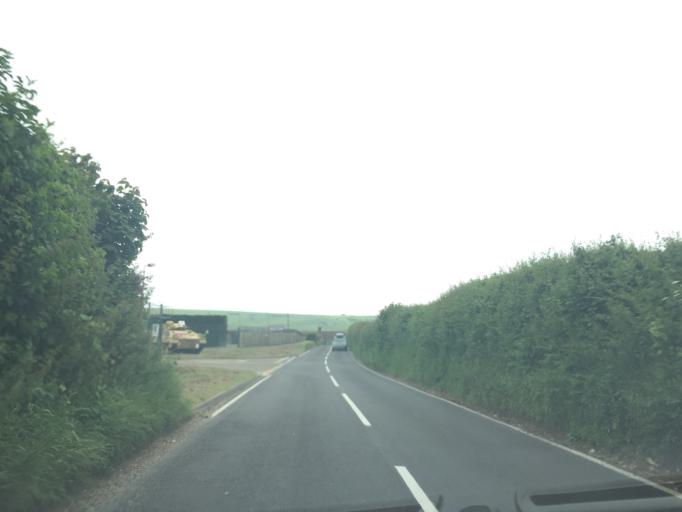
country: GB
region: England
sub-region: Dorset
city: Wool
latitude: 50.6331
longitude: -2.2346
